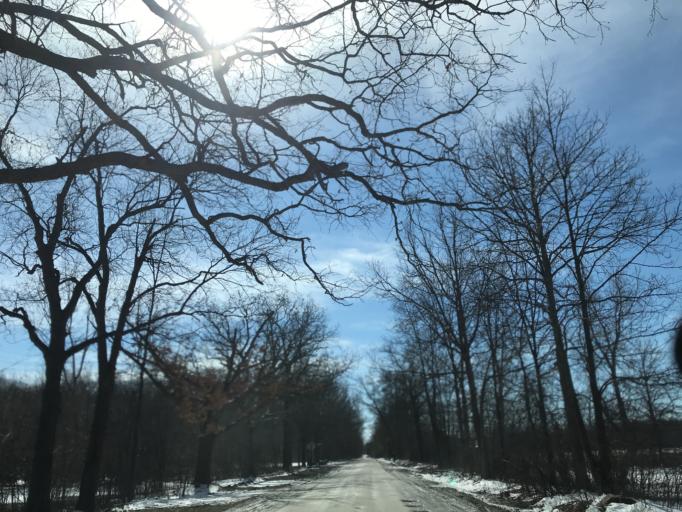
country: US
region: Michigan
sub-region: Livingston County
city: Whitmore Lake
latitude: 42.4282
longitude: -83.7249
